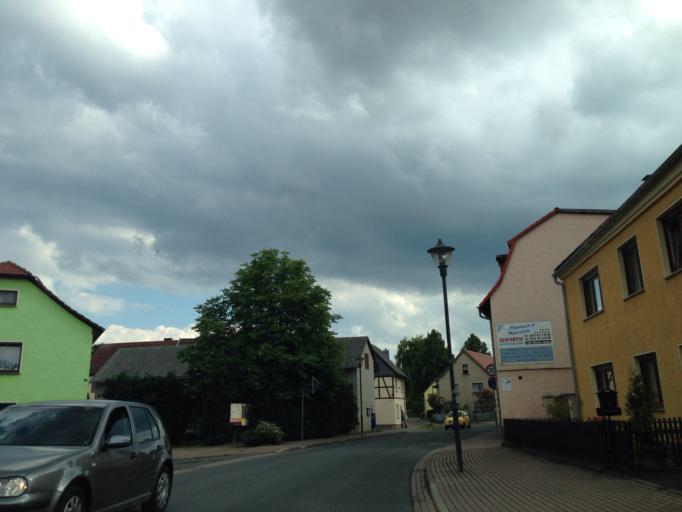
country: DE
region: Thuringia
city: Schwarza
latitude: 50.7864
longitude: 11.3121
